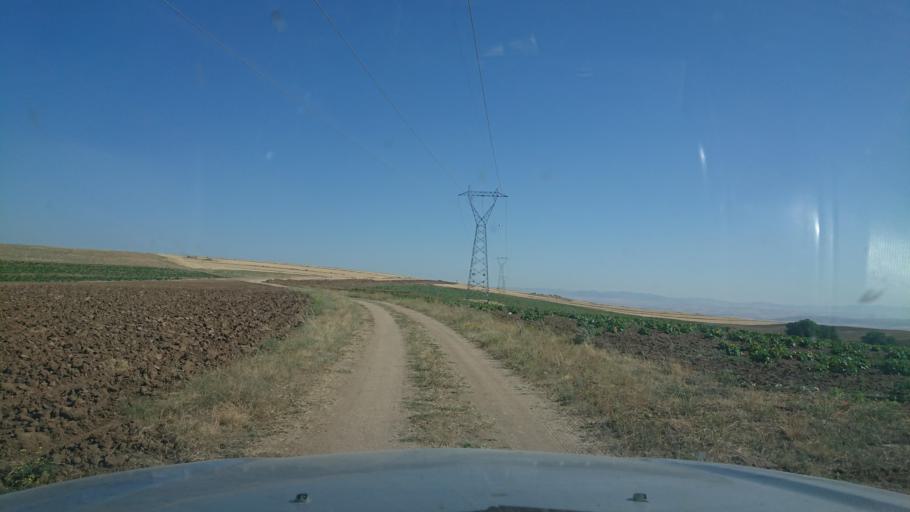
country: TR
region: Aksaray
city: Agacoren
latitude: 38.8357
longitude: 33.9453
